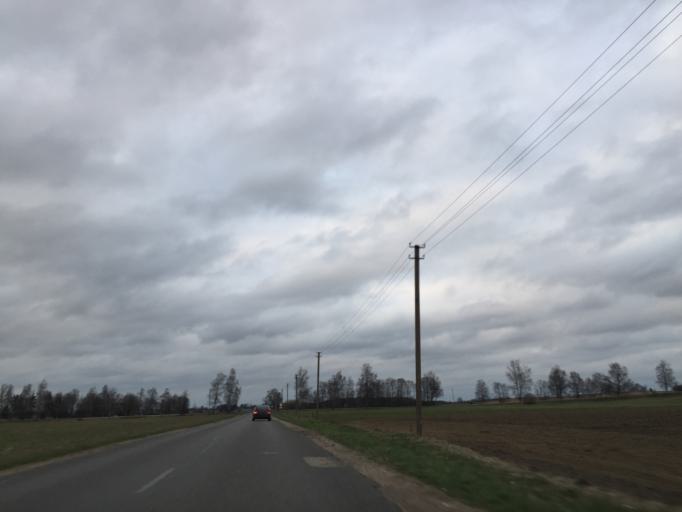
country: LT
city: Skaudvile
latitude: 55.4896
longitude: 22.5884
